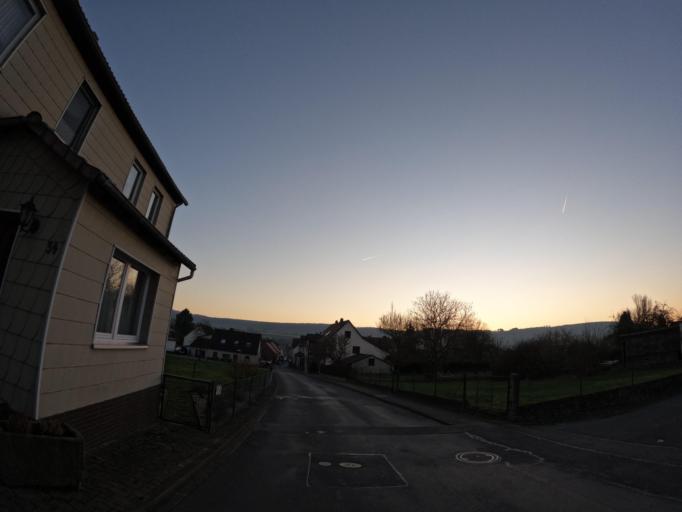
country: DE
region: Lower Saxony
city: Uslar
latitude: 51.6740
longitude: 9.6041
